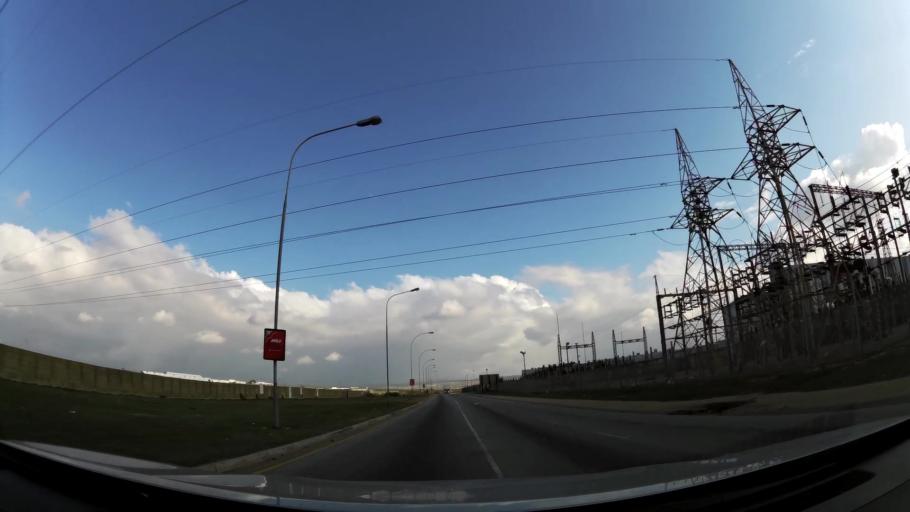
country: ZA
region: Eastern Cape
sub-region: Nelson Mandela Bay Metropolitan Municipality
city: Uitenhage
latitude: -33.7869
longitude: 25.4242
